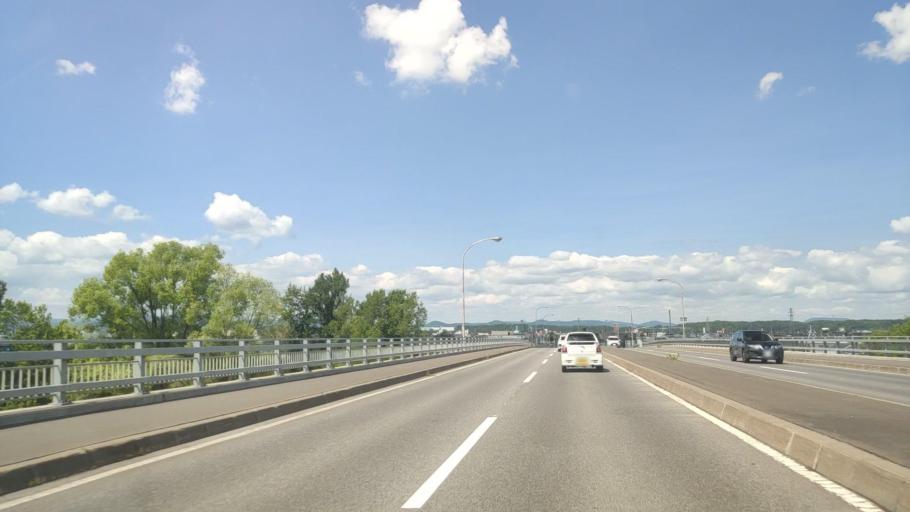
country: JP
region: Hokkaido
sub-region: Asahikawa-shi
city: Asahikawa
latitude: 43.7978
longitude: 142.3961
